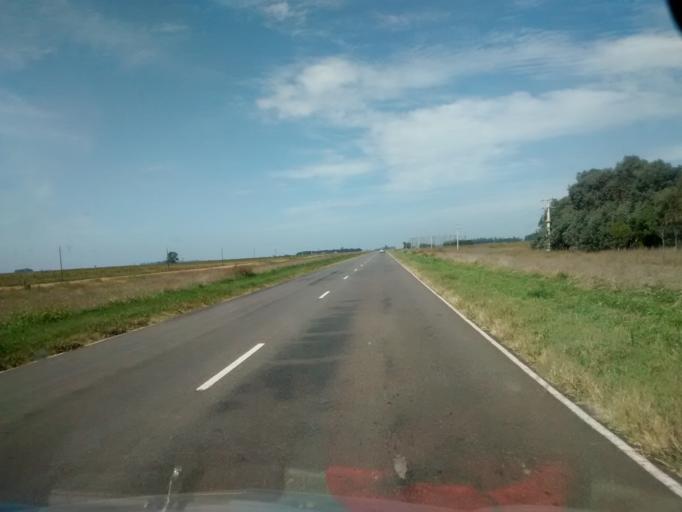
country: AR
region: Buenos Aires
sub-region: Partido de Ayacucho
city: Ayacucho
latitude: -36.8874
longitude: -58.5363
